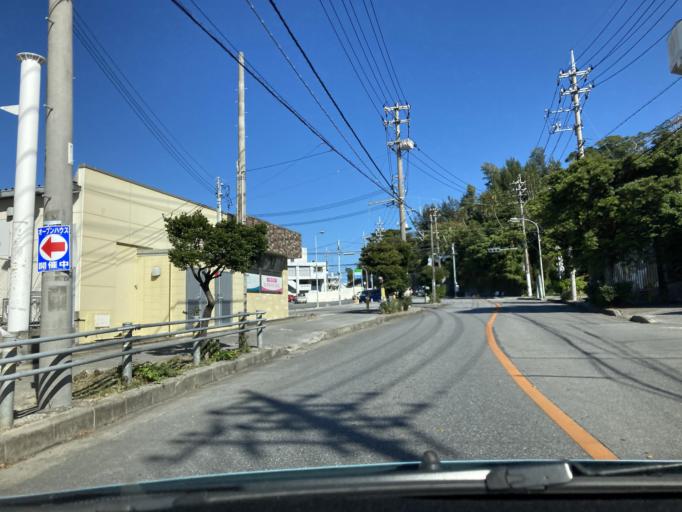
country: JP
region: Okinawa
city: Okinawa
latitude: 26.3256
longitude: 127.8014
